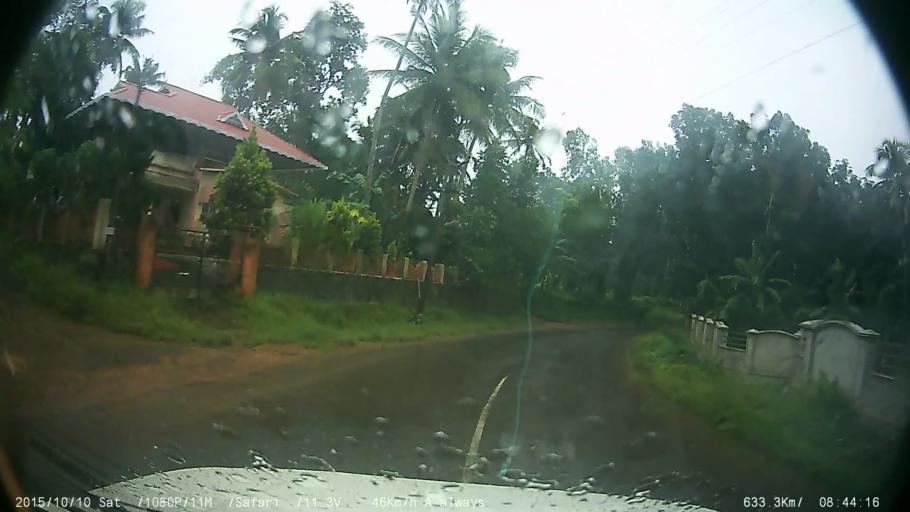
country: IN
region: Kerala
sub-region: Kottayam
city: Palackattumala
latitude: 9.7443
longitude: 76.5283
